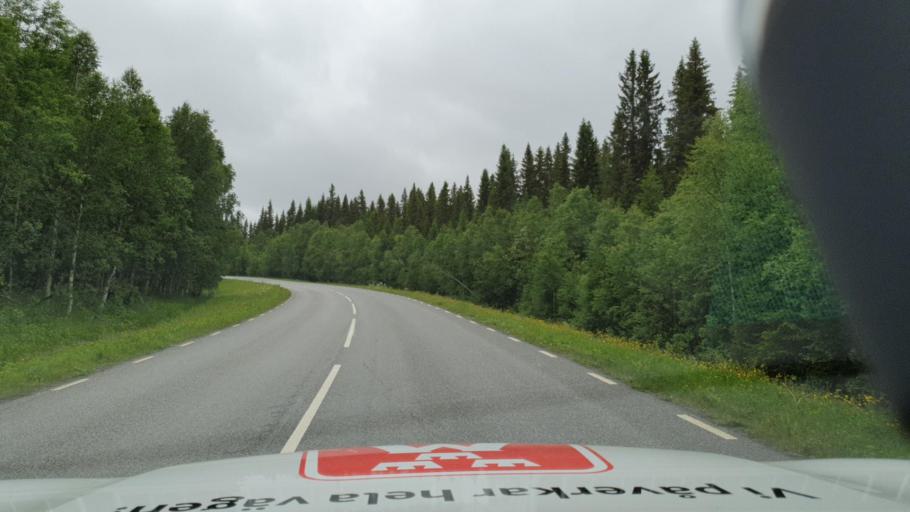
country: SE
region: Jaemtland
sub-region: Are Kommun
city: Are
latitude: 63.6777
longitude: 13.0503
